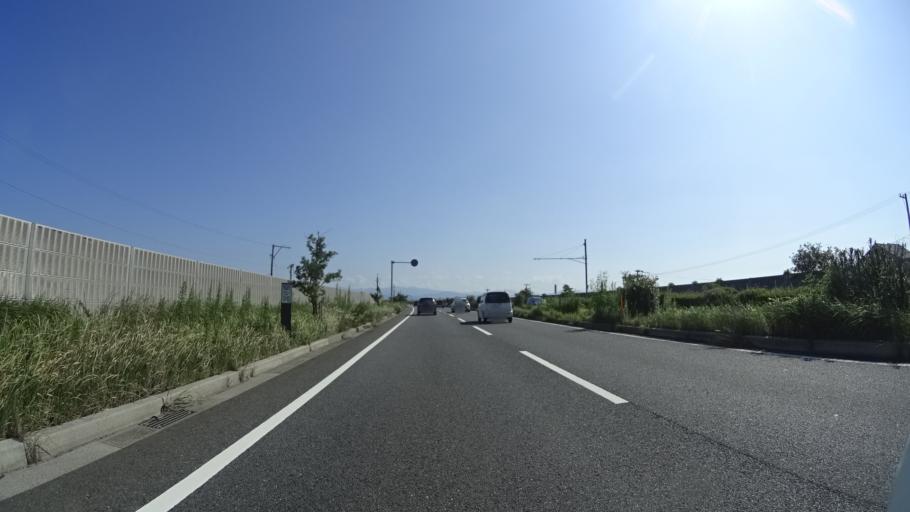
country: JP
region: Fukuoka
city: Yukuhashi
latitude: 33.7251
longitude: 130.9927
